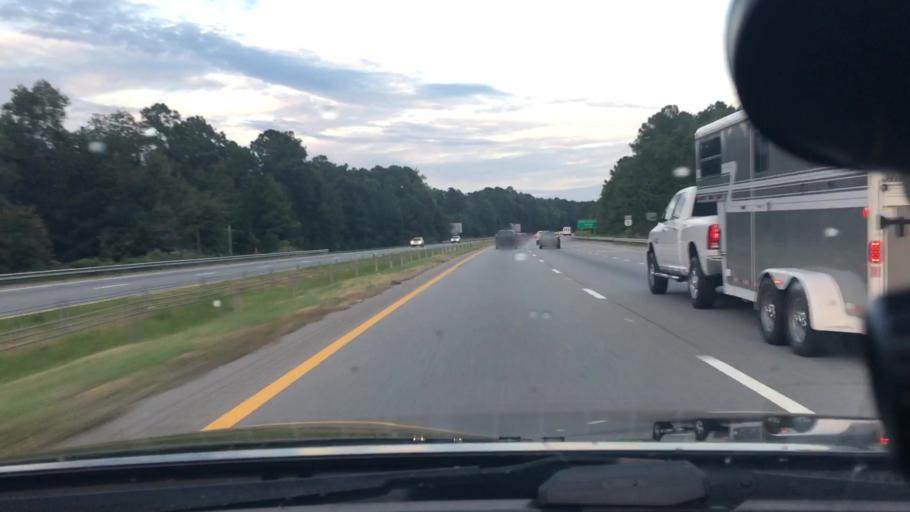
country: US
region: North Carolina
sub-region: Wake County
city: Apex
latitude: 35.7197
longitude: -78.8339
